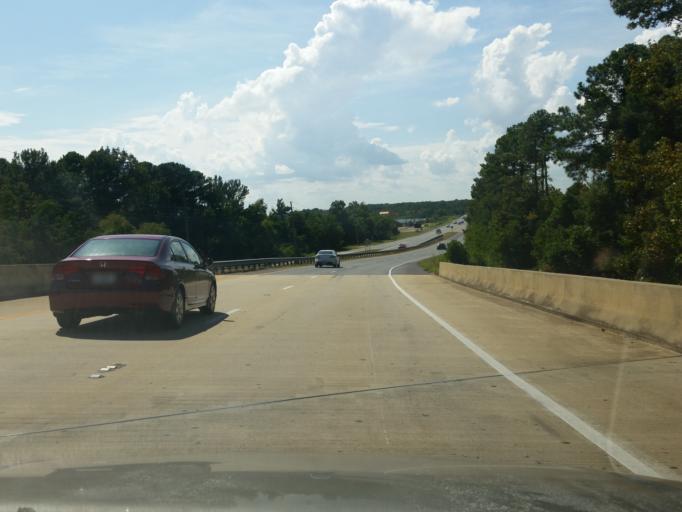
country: US
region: Alabama
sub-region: Baldwin County
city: Spanish Fort
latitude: 30.6669
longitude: -87.9171
